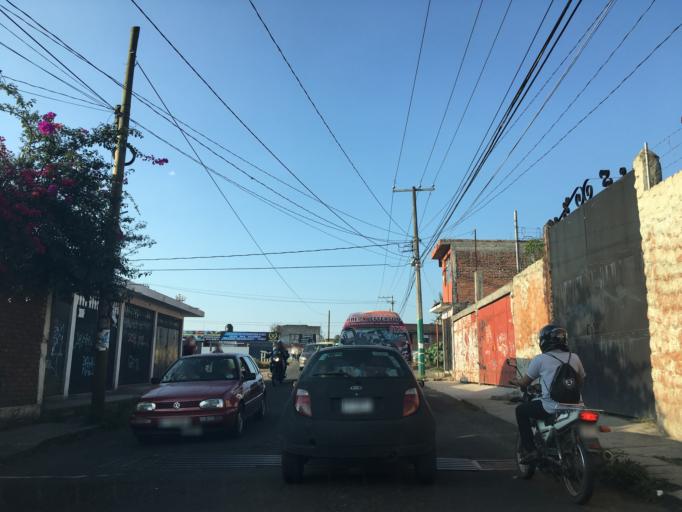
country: MX
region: Michoacan
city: Morelia
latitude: 19.6919
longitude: -101.2260
